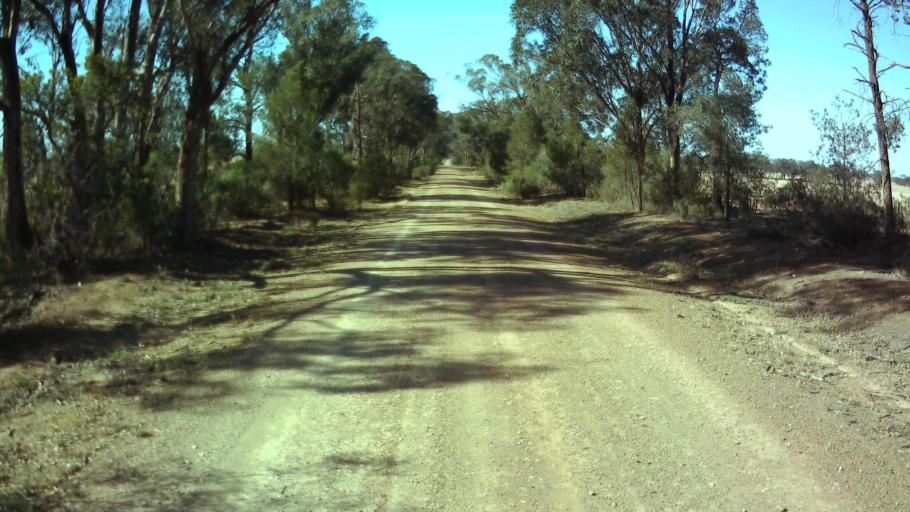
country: AU
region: New South Wales
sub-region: Weddin
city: Grenfell
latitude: -33.9112
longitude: 147.8767
